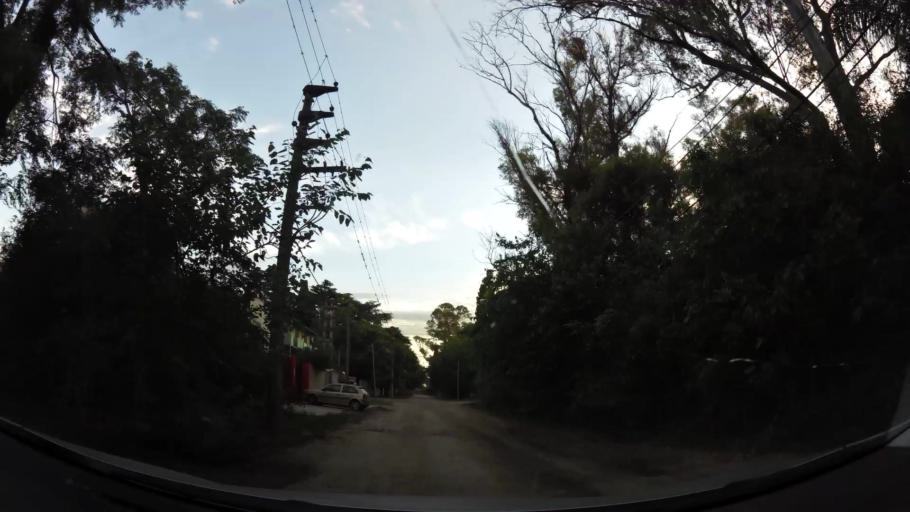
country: AR
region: Buenos Aires
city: Santa Catalina - Dique Lujan
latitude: -34.4515
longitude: -58.6632
